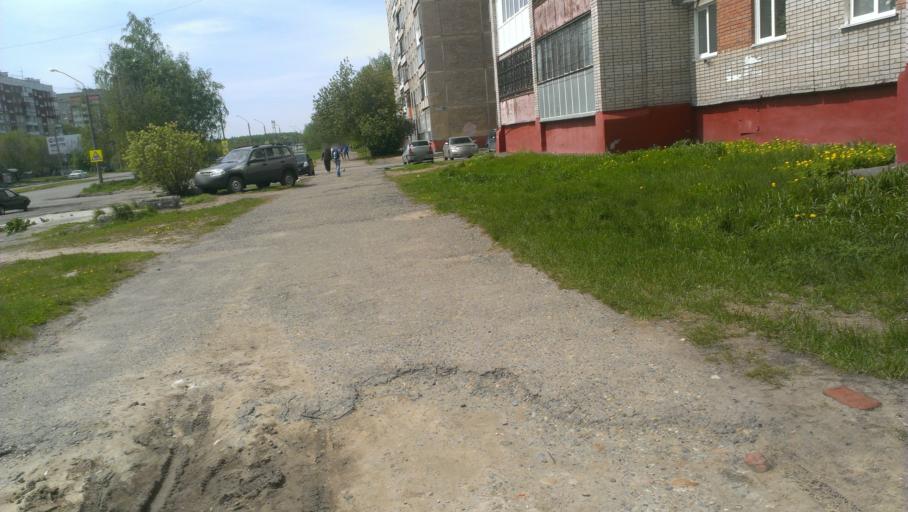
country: RU
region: Altai Krai
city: Novosilikatnyy
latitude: 53.3626
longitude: 83.6723
